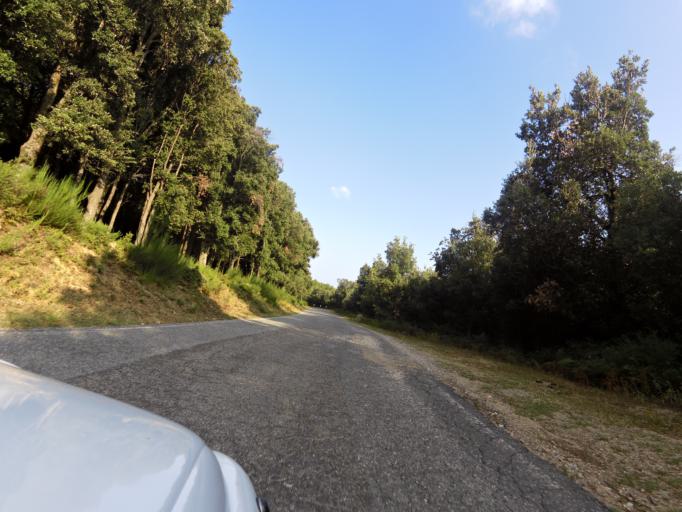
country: IT
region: Calabria
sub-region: Provincia di Reggio Calabria
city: Pazzano
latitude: 38.4742
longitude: 16.4010
